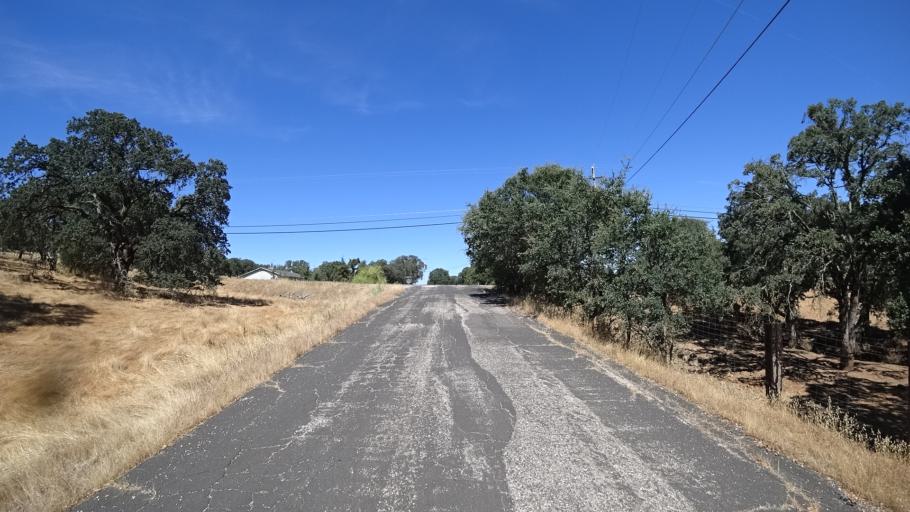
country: US
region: California
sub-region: Calaveras County
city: Rancho Calaveras
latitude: 38.1555
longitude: -120.8397
